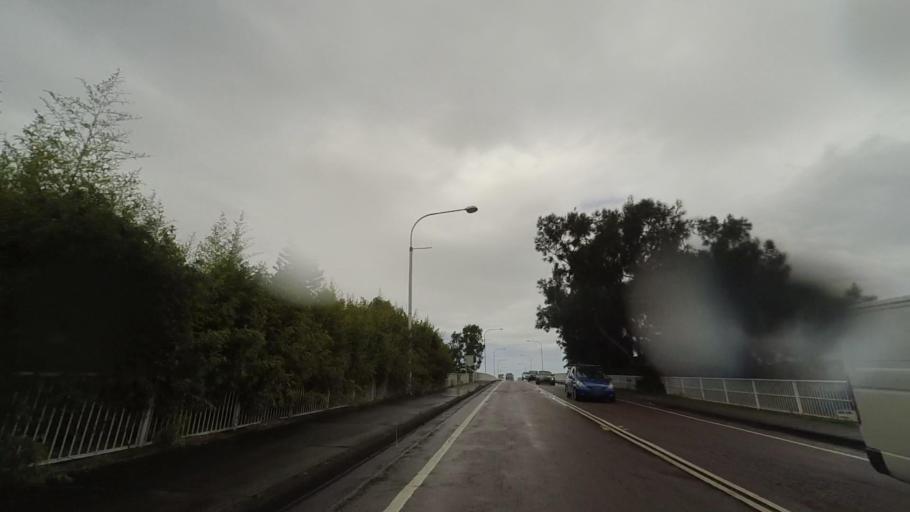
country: AU
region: New South Wales
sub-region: Wyong Shire
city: The Entrance
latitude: -33.3394
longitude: 151.4979
